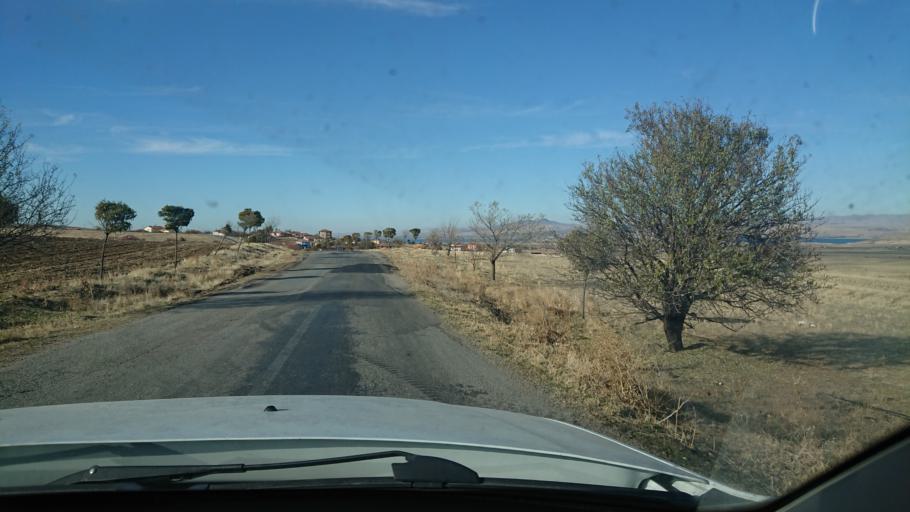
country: TR
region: Aksaray
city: Sariyahsi
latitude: 38.9748
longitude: 33.8581
